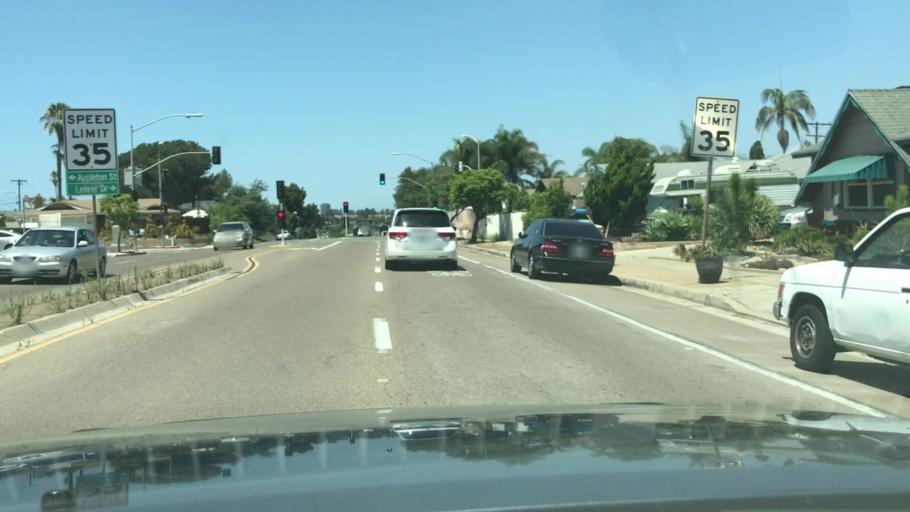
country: US
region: California
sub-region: San Diego County
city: La Jolla
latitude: 32.8380
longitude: -117.1960
